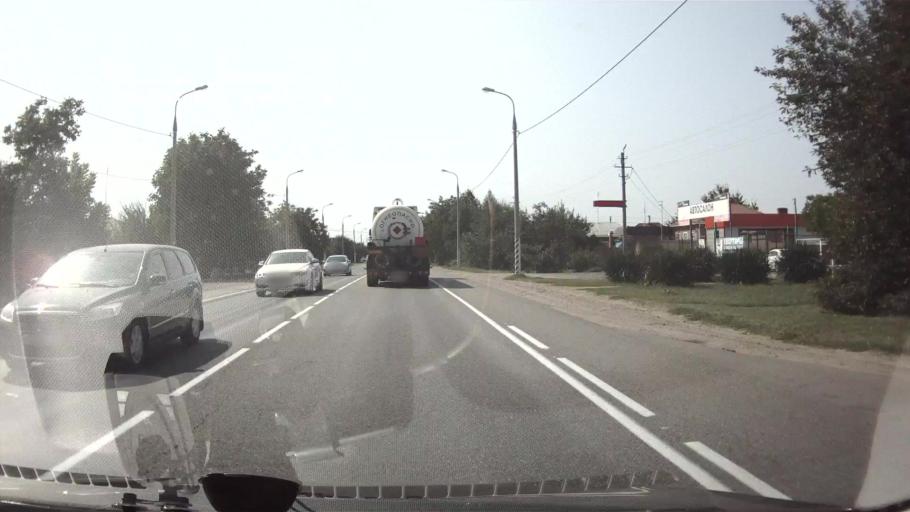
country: RU
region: Adygeya
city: Krasnogvardeyskoye
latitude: 45.2145
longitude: 39.5563
